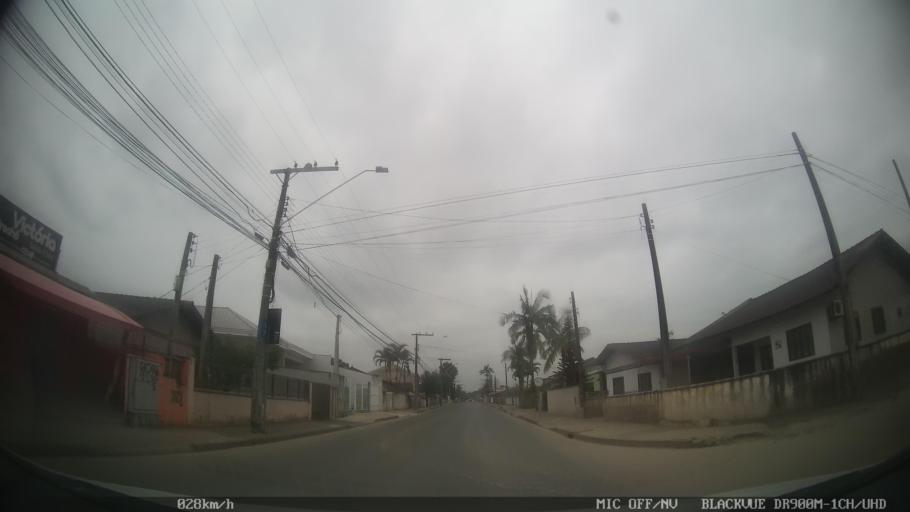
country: BR
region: Santa Catarina
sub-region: Joinville
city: Joinville
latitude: -26.3565
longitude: -48.8281
